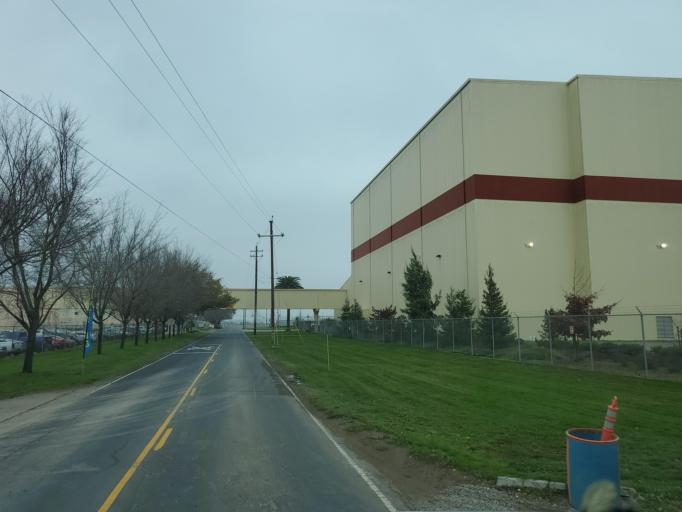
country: US
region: California
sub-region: San Joaquin County
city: Lathrop
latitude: 37.8234
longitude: -121.2720
